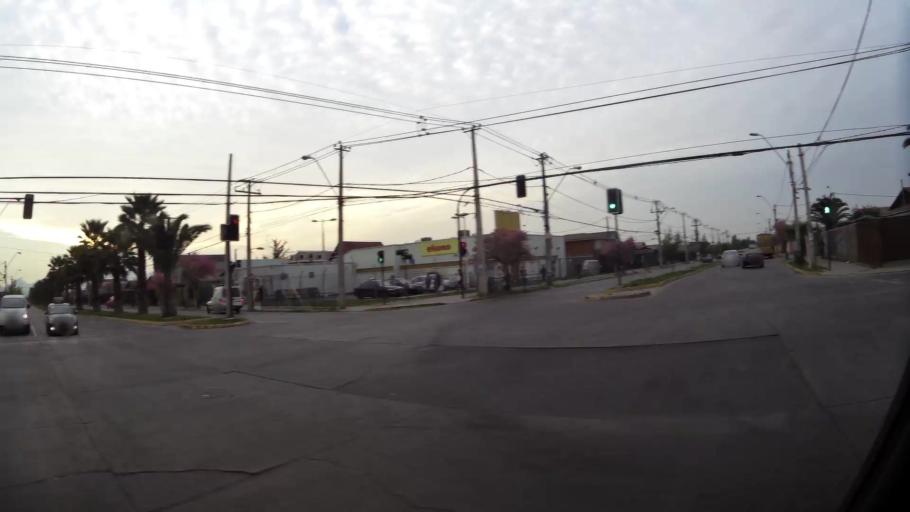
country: CL
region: Santiago Metropolitan
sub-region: Provincia de Santiago
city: Lo Prado
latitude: -33.5249
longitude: -70.7918
